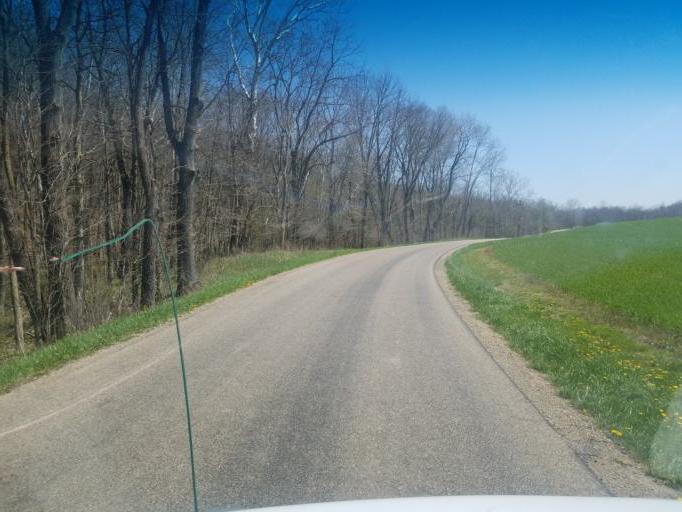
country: US
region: Ohio
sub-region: Knox County
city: Gambier
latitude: 40.3937
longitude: -82.3224
